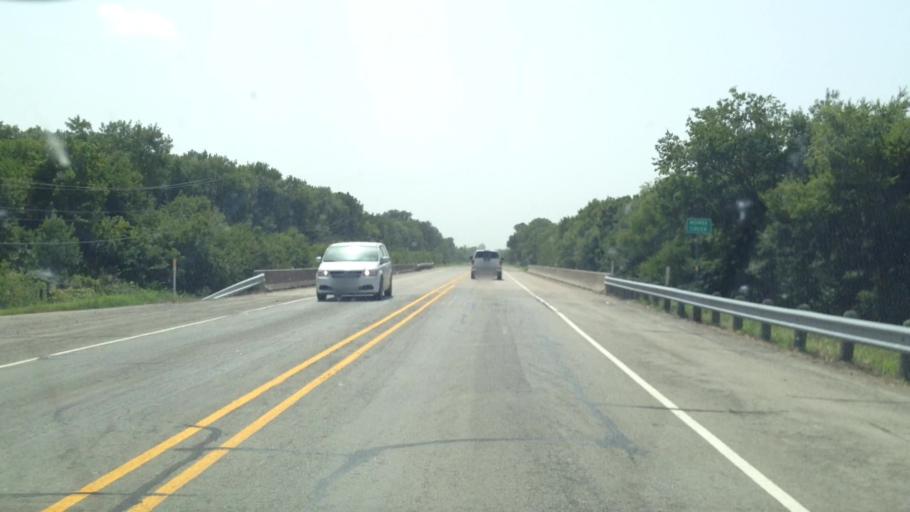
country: US
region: Texas
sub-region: Hunt County
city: Greenville
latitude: 33.1395
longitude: -96.0816
